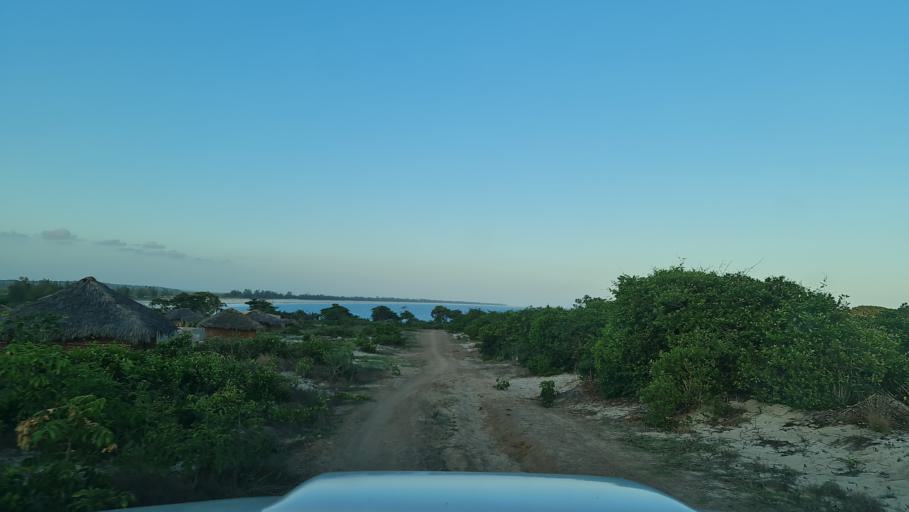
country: MZ
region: Nampula
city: Ilha de Mocambique
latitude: -15.6294
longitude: 40.4213
